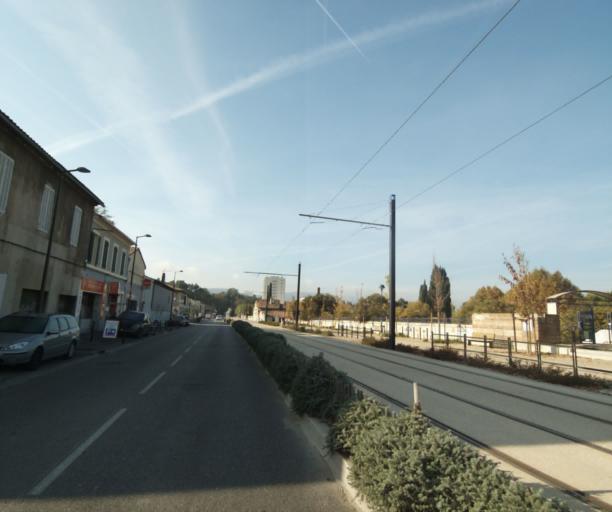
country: FR
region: Provence-Alpes-Cote d'Azur
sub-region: Departement des Bouches-du-Rhone
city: Aubagne
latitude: 43.2924
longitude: 5.5621
